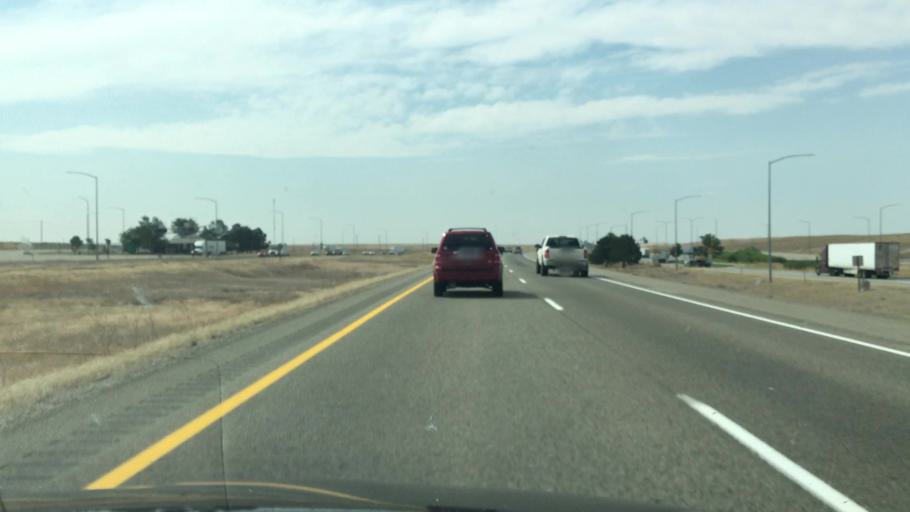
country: US
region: Idaho
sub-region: Ada County
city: Boise
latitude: 43.4303
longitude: -116.0546
